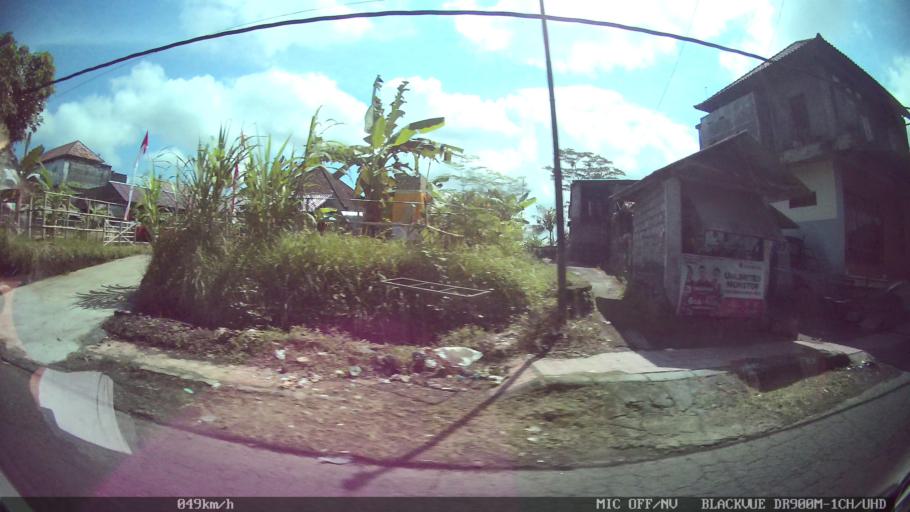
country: ID
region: Bali
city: Banjar Kelodan
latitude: -8.5246
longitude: 115.3286
